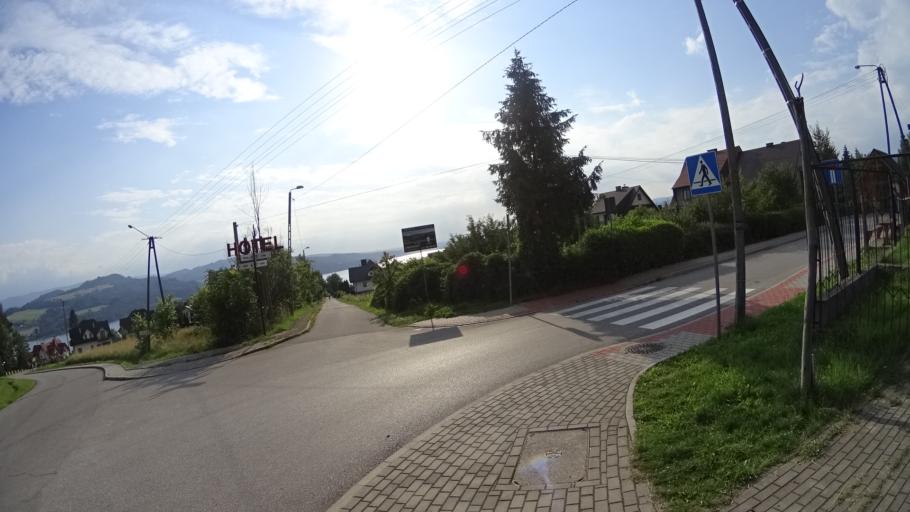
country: PL
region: Lesser Poland Voivodeship
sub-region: Powiat nowotarski
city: Krosnica
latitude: 49.4373
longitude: 20.3254
